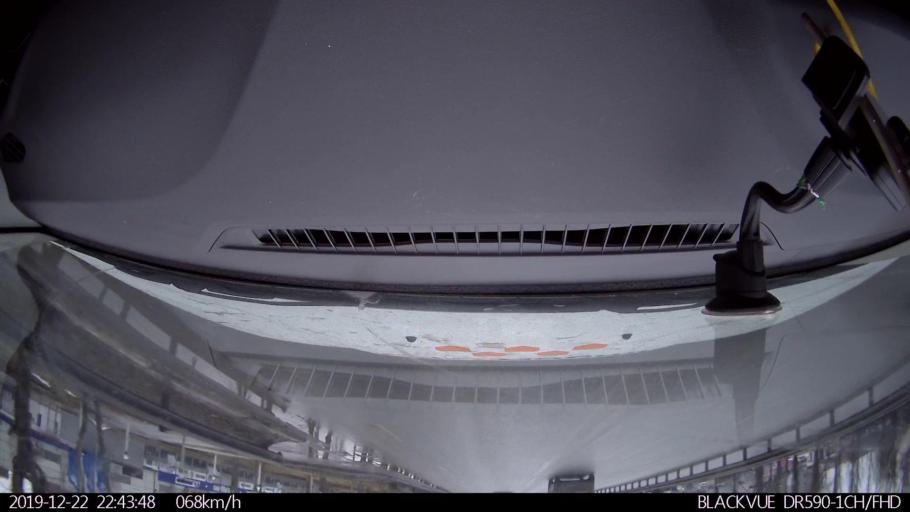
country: RU
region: Nizjnij Novgorod
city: Nizhniy Novgorod
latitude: 56.2788
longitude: 43.9006
